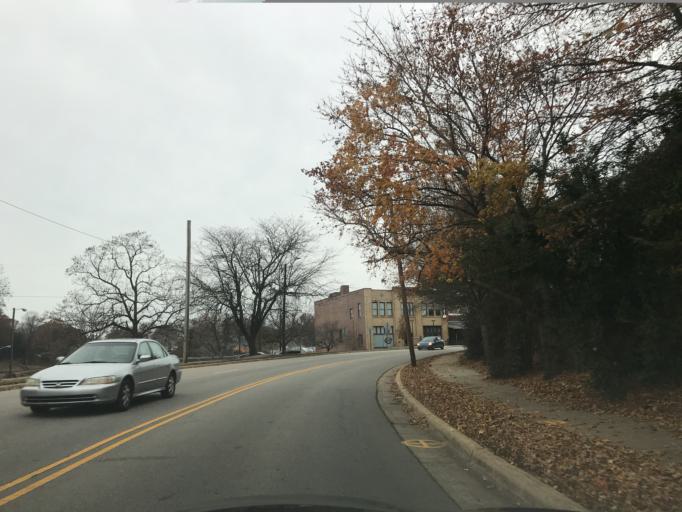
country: US
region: North Carolina
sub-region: Wake County
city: West Raleigh
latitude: 35.7801
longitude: -78.6553
